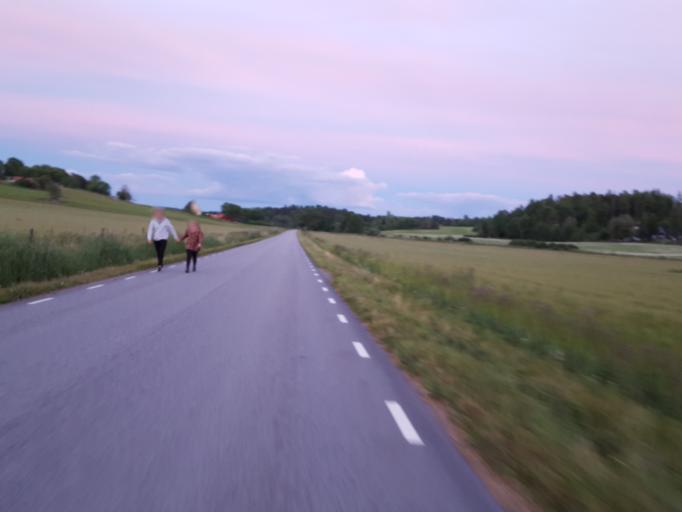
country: SE
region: Uppsala
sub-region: Uppsala Kommun
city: Uppsala
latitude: 59.7908
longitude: 17.5857
